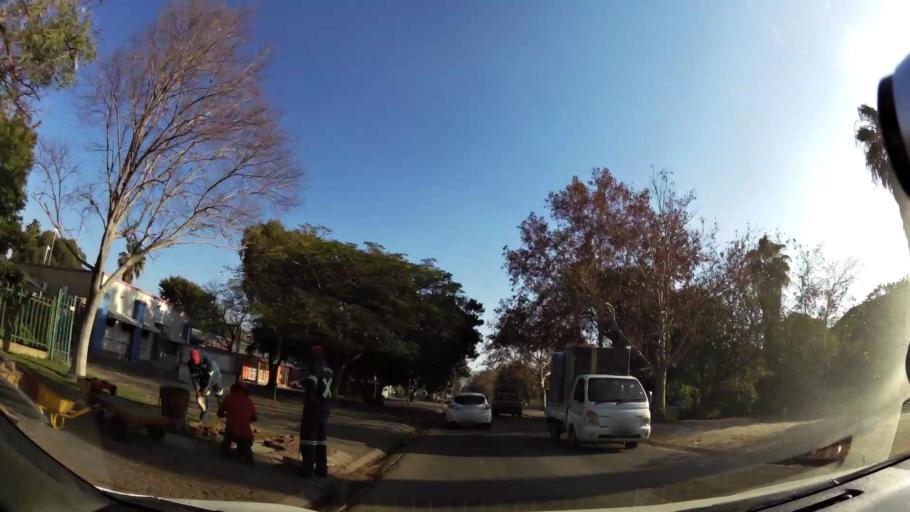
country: ZA
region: North-West
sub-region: Bojanala Platinum District Municipality
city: Rustenburg
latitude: -25.6742
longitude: 27.2386
